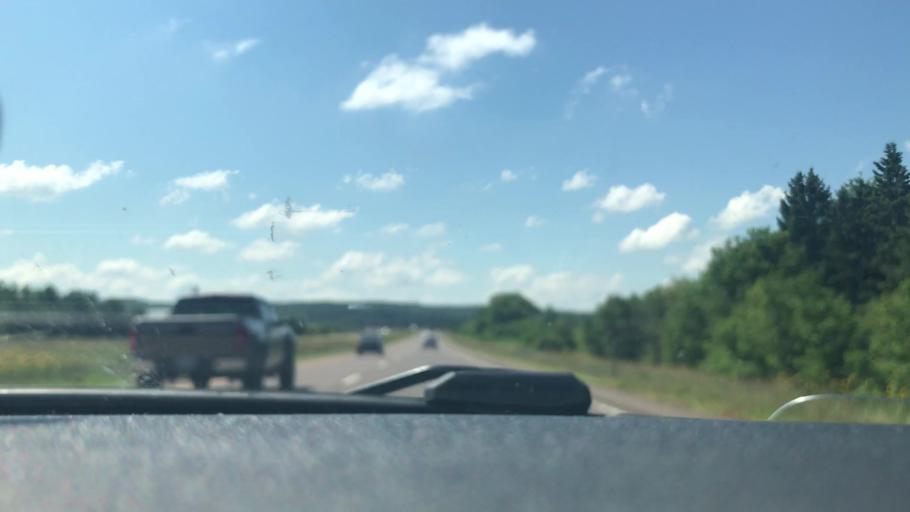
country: US
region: Wisconsin
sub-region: Chippewa County
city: Chippewa Falls
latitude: 44.9948
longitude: -91.4425
